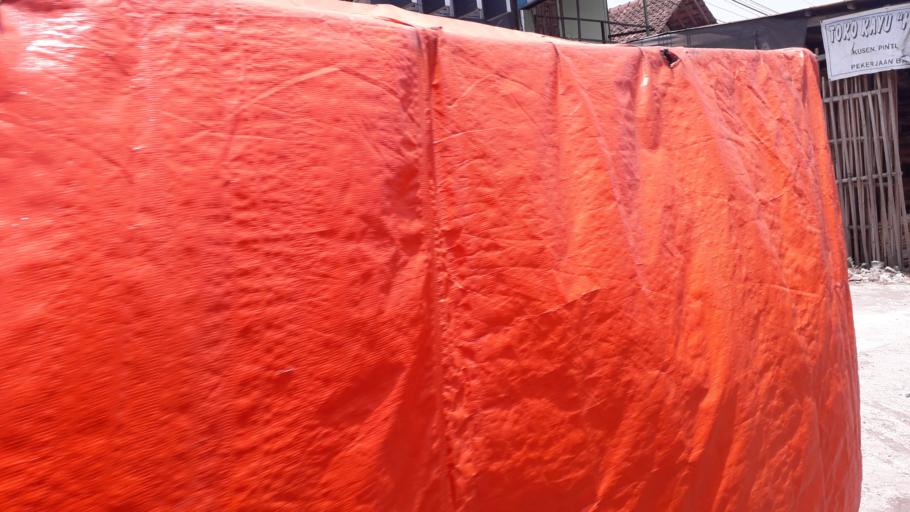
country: ID
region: Daerah Istimewa Yogyakarta
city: Yogyakarta
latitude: -7.7651
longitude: 110.3691
